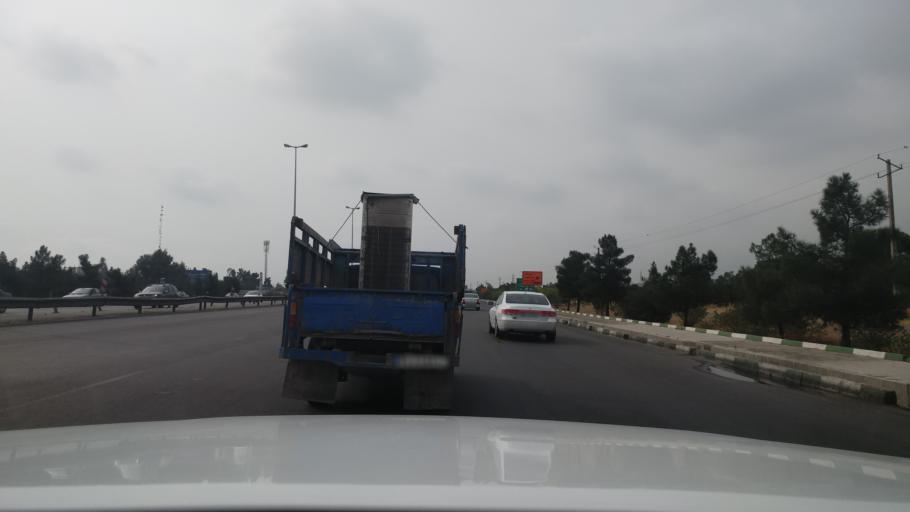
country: IR
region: Tehran
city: Shahr-e Qods
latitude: 35.7149
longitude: 51.2598
